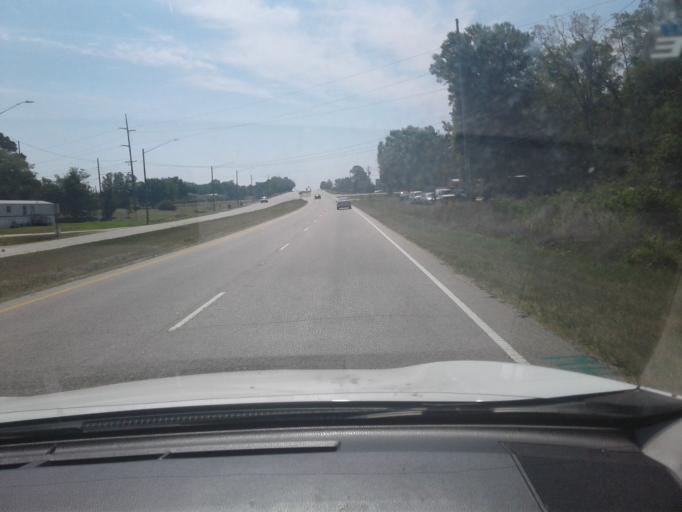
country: US
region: North Carolina
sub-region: Harnett County
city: Erwin
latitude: 35.3322
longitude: -78.6686
